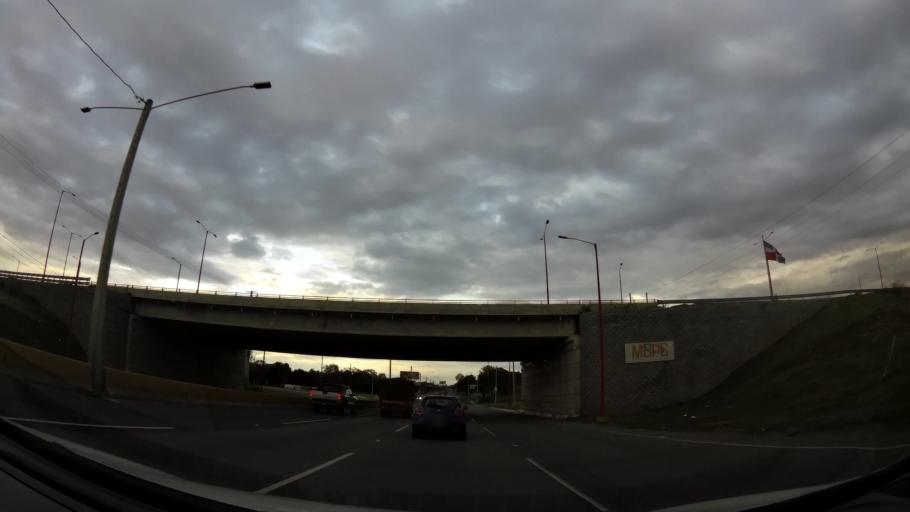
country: DO
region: Santo Domingo
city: Santo Domingo Oeste
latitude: 18.5626
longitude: -70.0696
